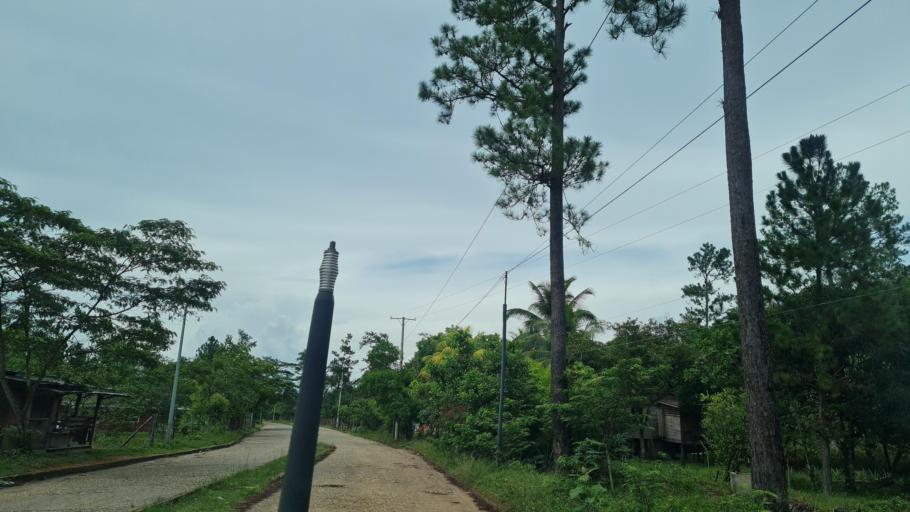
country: NI
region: Atlantico Norte (RAAN)
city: Waspam
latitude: 14.7265
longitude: -83.9715
